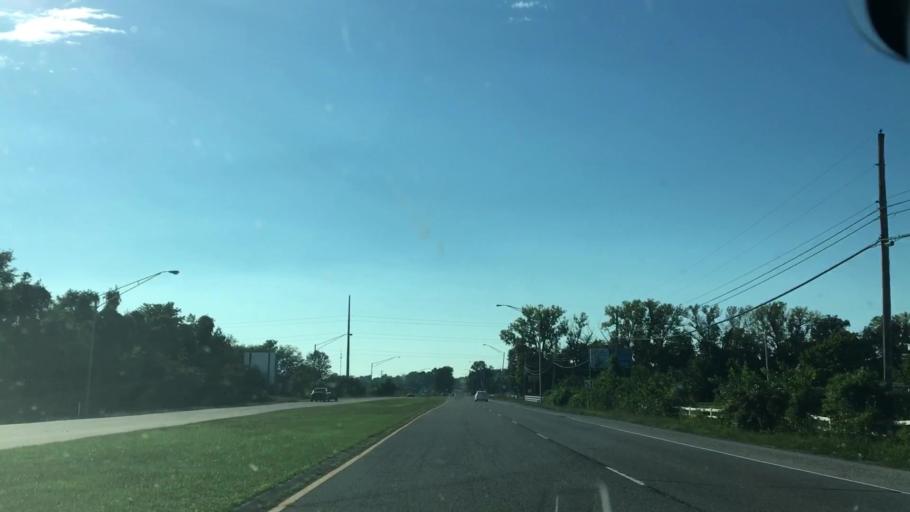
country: US
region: Kentucky
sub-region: Daviess County
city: Owensboro
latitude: 37.7757
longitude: -87.1675
